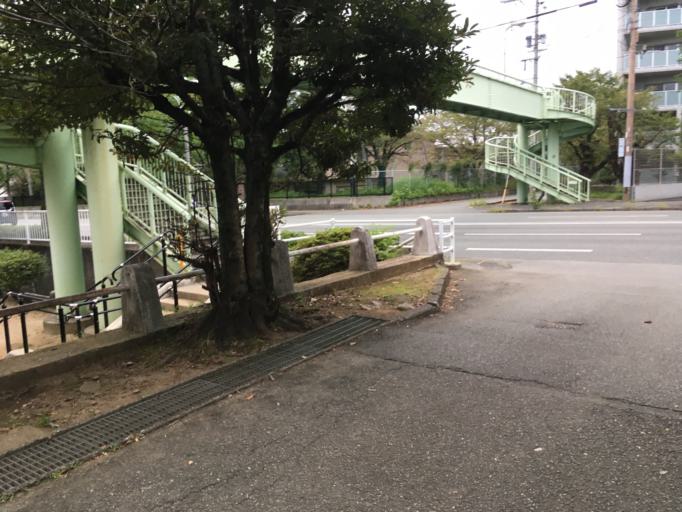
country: JP
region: Kumamoto
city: Kumamoto
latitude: 32.8068
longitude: 130.7333
